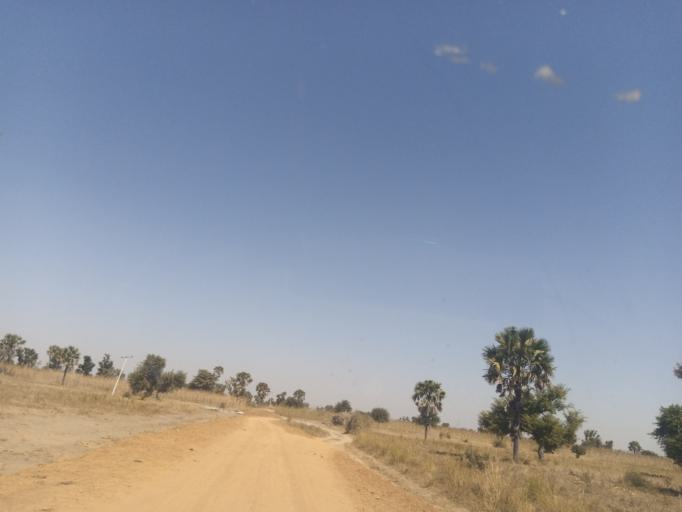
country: NG
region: Adamawa
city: Yola
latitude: 9.2952
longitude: 12.8864
